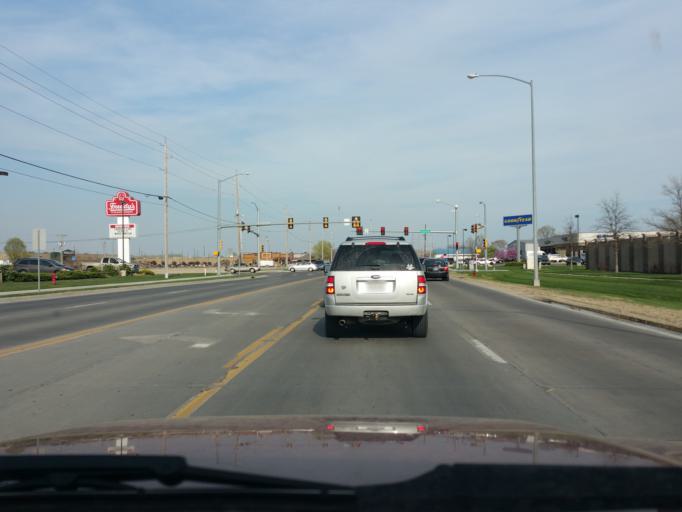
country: US
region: Kansas
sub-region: Riley County
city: Manhattan
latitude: 39.1895
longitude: -96.5560
